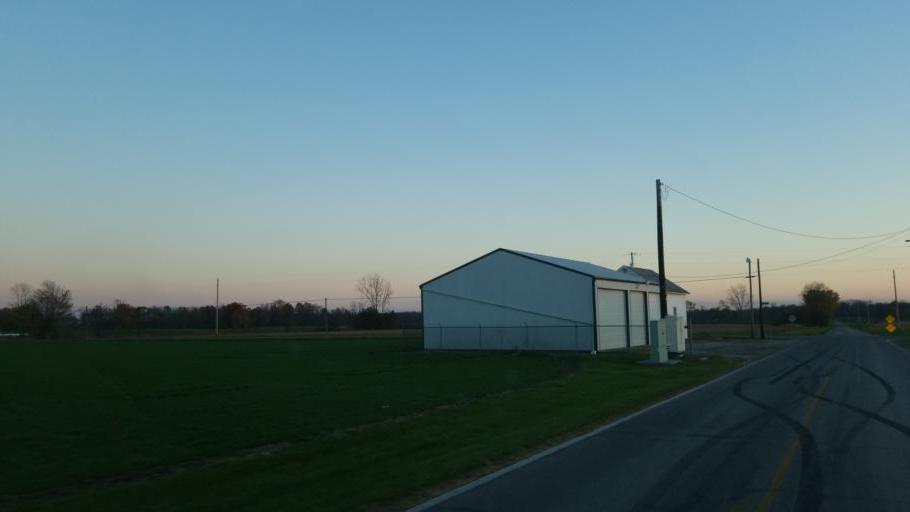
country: US
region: Ohio
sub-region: Huron County
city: Willard
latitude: 41.0339
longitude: -82.7820
